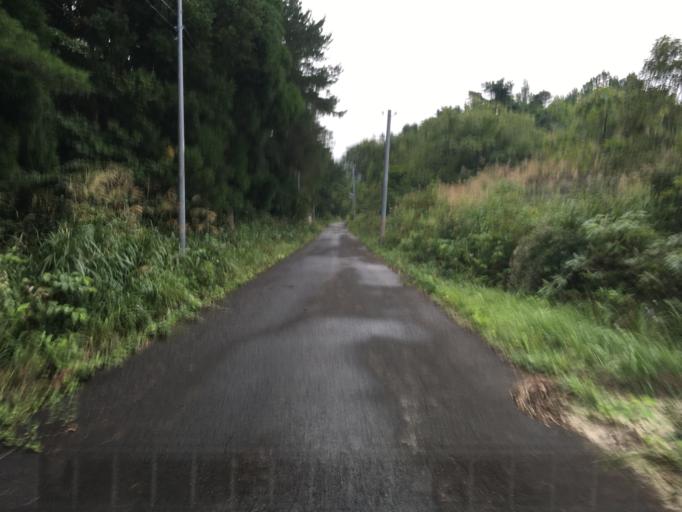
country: JP
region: Fukushima
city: Fukushima-shi
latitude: 37.8093
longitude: 140.3430
